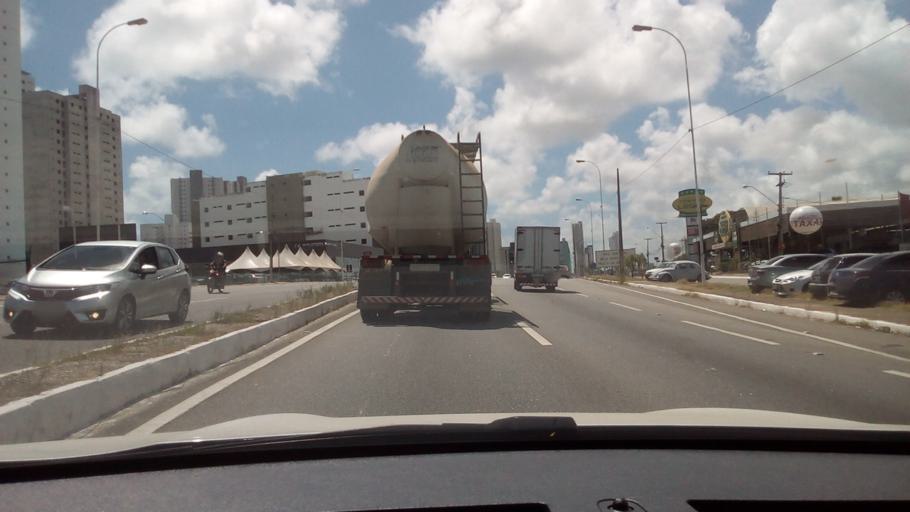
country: BR
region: Paraiba
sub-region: Joao Pessoa
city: Joao Pessoa
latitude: -7.1060
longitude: -34.8442
